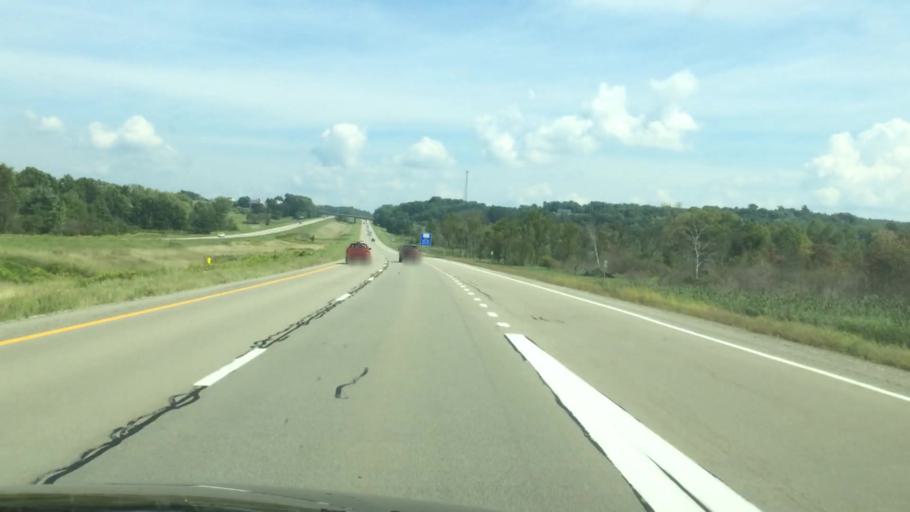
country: US
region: Pennsylvania
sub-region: Erie County
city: North East
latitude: 42.1316
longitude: -79.7374
